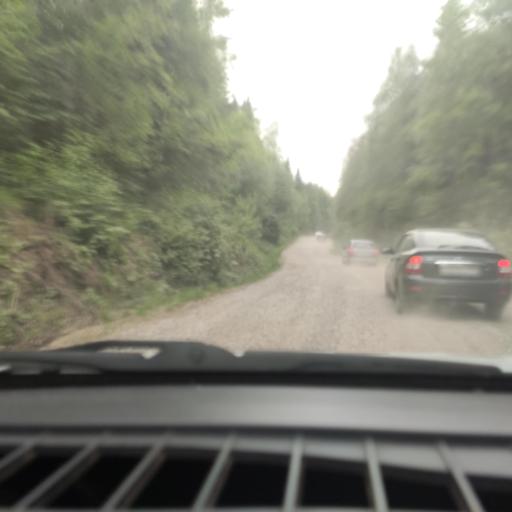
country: RU
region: Perm
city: Novyye Lyady
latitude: 57.9071
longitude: 56.6559
